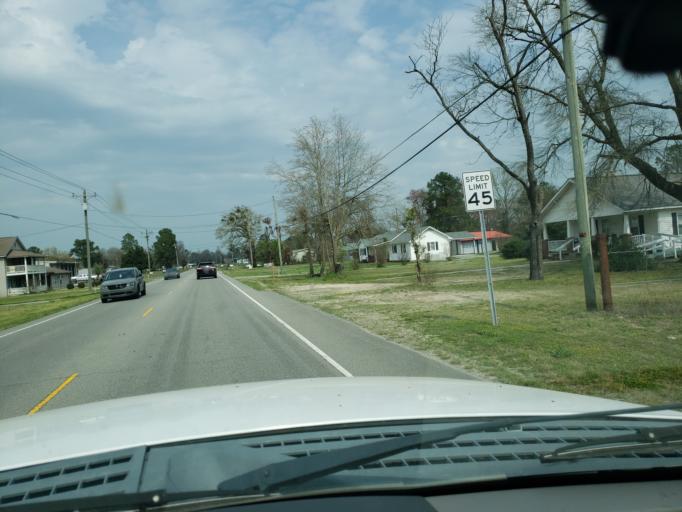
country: US
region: North Carolina
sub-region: Duplin County
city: Wallace
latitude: 34.7804
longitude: -77.9109
